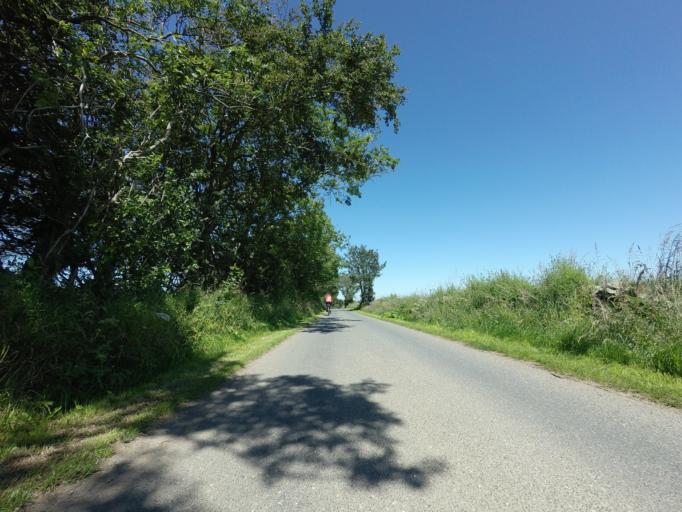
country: GB
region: Scotland
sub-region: Aberdeenshire
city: Macduff
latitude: 57.6558
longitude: -2.4997
